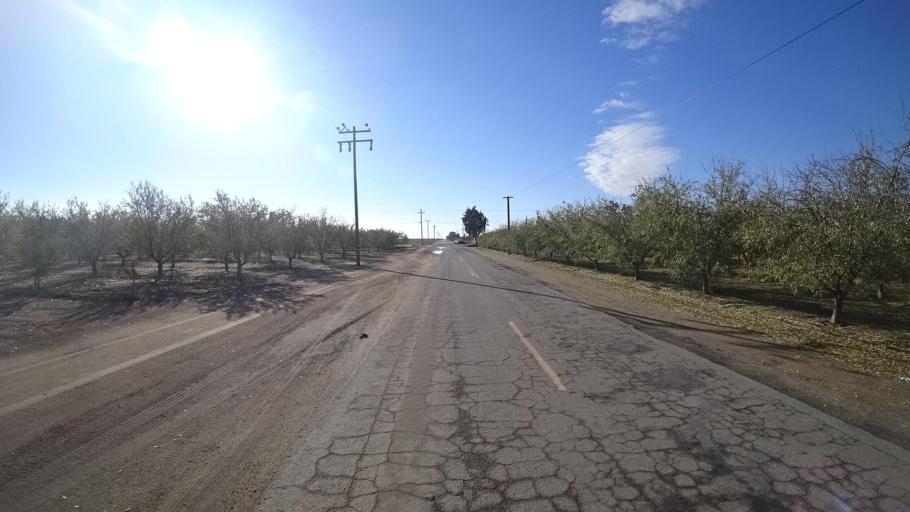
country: US
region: California
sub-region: Kern County
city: Delano
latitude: 35.7189
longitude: -119.3119
